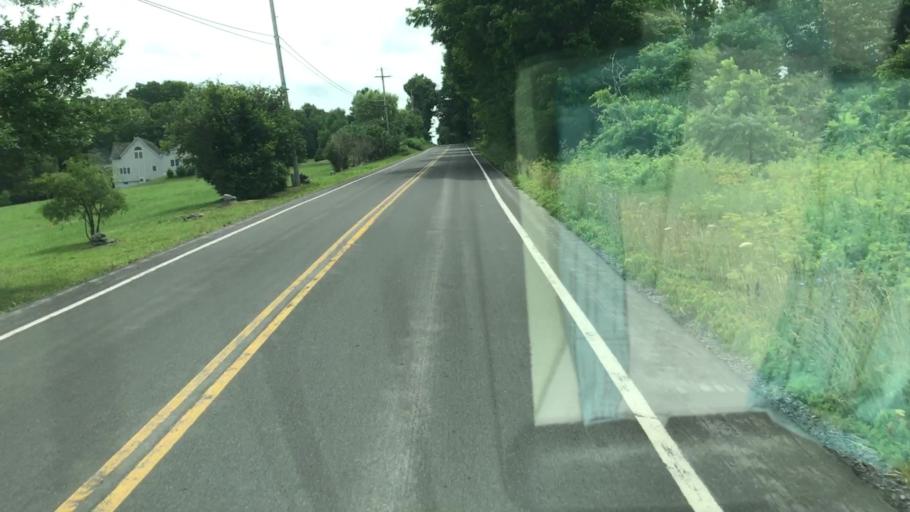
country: US
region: New York
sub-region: Onondaga County
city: Manlius
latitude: 42.9448
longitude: -75.9800
